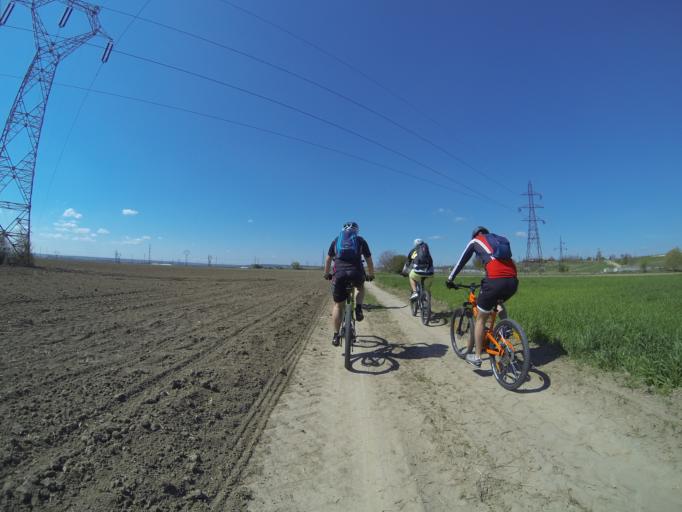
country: RO
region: Dolj
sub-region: Comuna Isalnita
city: Isalnita
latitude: 44.3896
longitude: 23.7527
